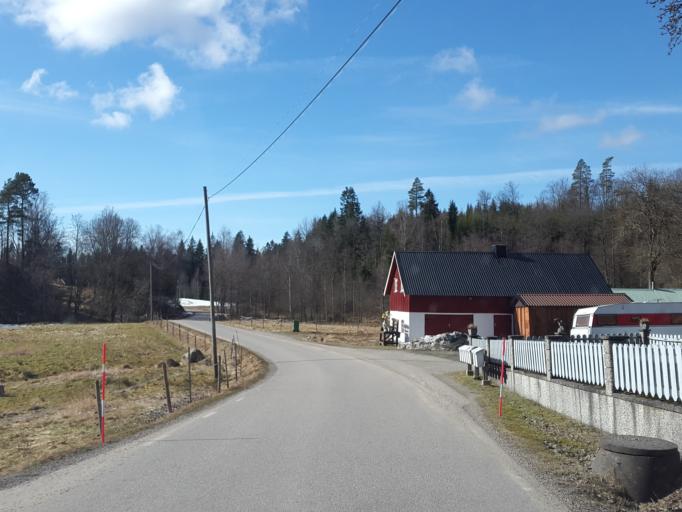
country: SE
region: Vaestra Goetaland
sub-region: Boras Kommun
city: Boras
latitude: 57.7697
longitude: 12.9348
